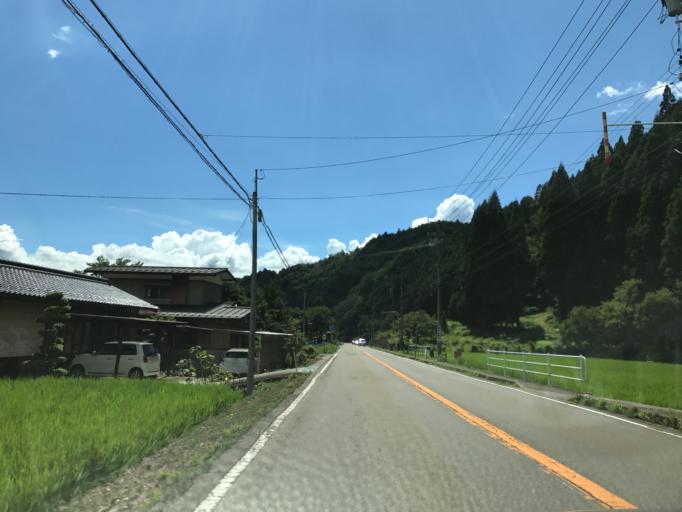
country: JP
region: Gifu
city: Gujo
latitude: 35.7826
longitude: 137.0040
